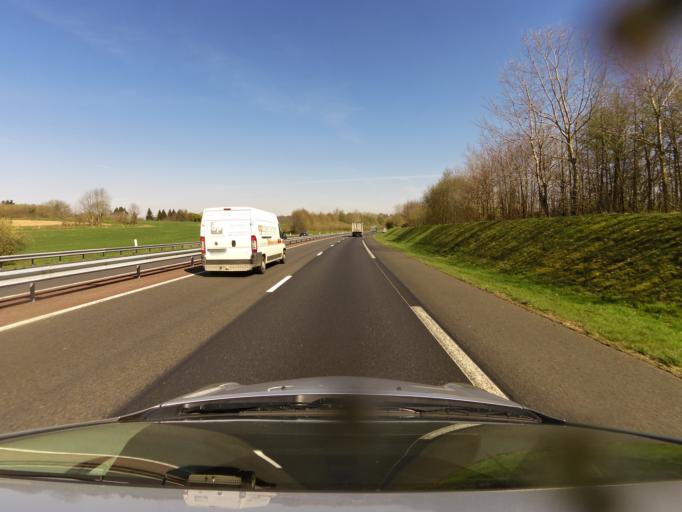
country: FR
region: Lower Normandy
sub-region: Departement de la Manche
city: Villedieu-les-Poeles
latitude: 48.7972
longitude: -1.2641
